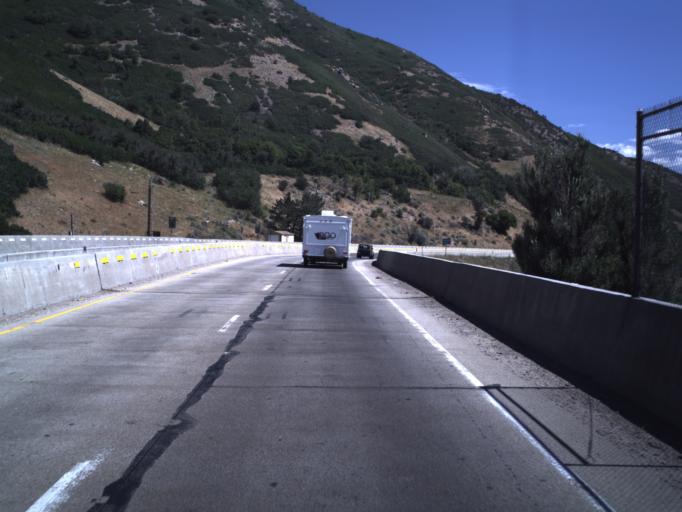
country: US
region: Utah
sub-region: Morgan County
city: Mountain Green
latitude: 41.1388
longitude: -111.8556
